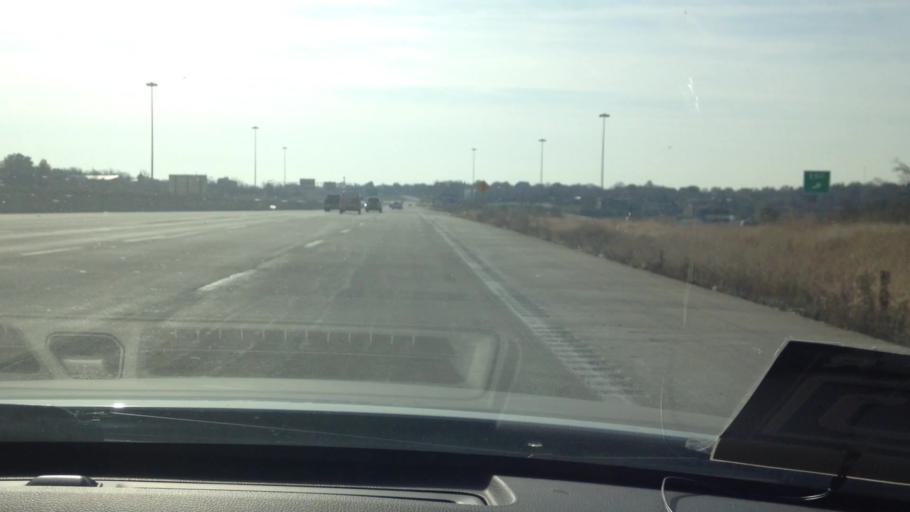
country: US
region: Missouri
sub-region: Jackson County
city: Grandview
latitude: 38.9287
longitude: -94.5279
